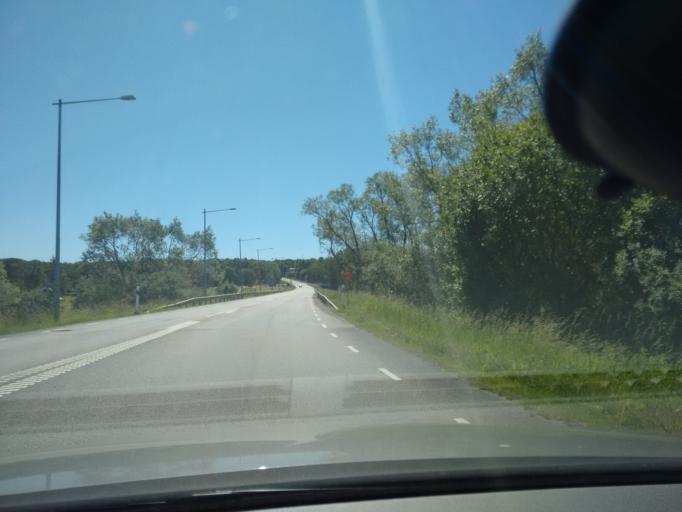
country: SE
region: Skane
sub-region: Horby Kommun
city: Hoerby
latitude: 55.8487
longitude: 13.6458
